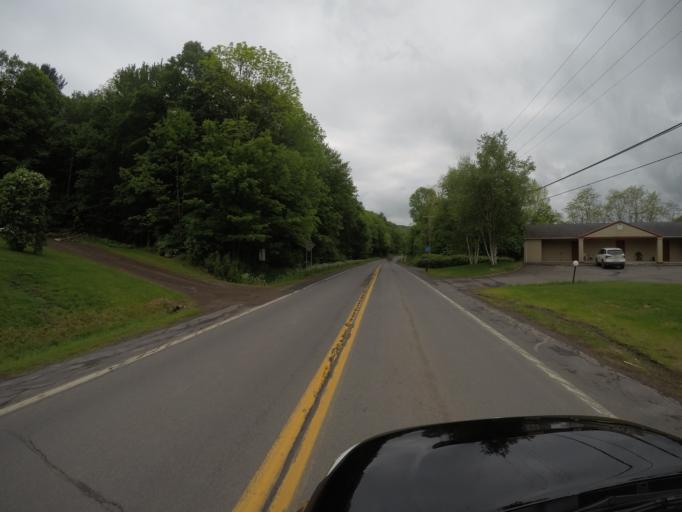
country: US
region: New York
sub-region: Delaware County
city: Delhi
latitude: 42.2646
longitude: -74.9185
